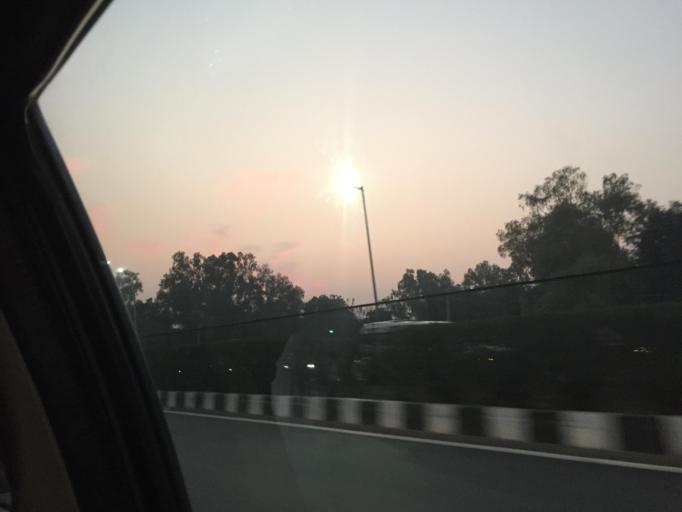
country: IN
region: Haryana
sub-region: Gurgaon
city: Gurgaon
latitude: 28.5196
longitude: 77.0971
